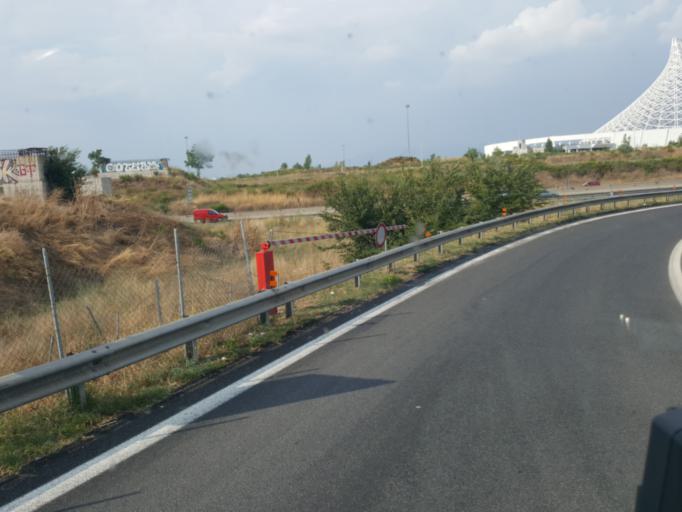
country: IT
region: Latium
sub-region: Citta metropolitana di Roma Capitale
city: Frascati
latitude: 41.8400
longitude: 12.6313
